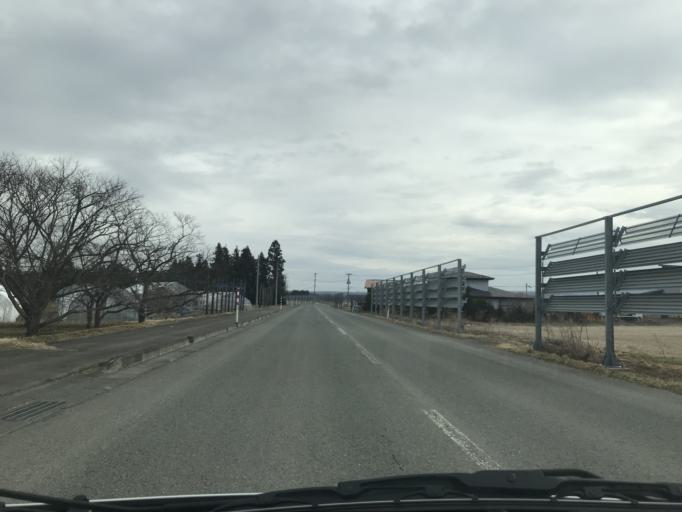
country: JP
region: Iwate
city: Kitakami
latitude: 39.3316
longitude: 140.9953
